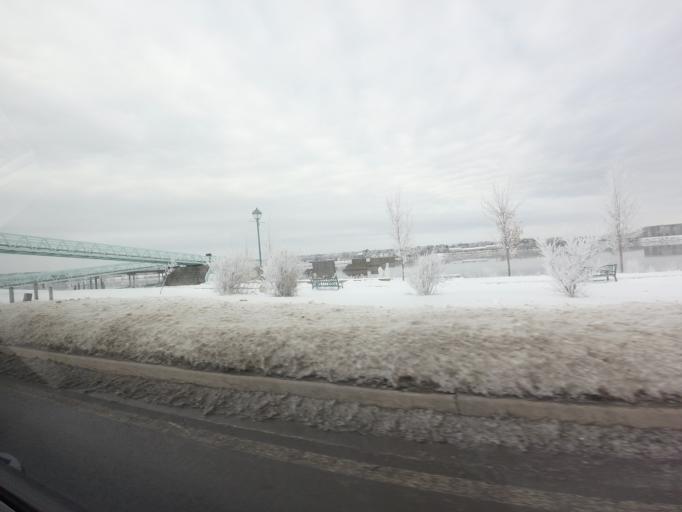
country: CA
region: New Brunswick
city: Fredericton
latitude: 45.9632
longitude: -66.6395
